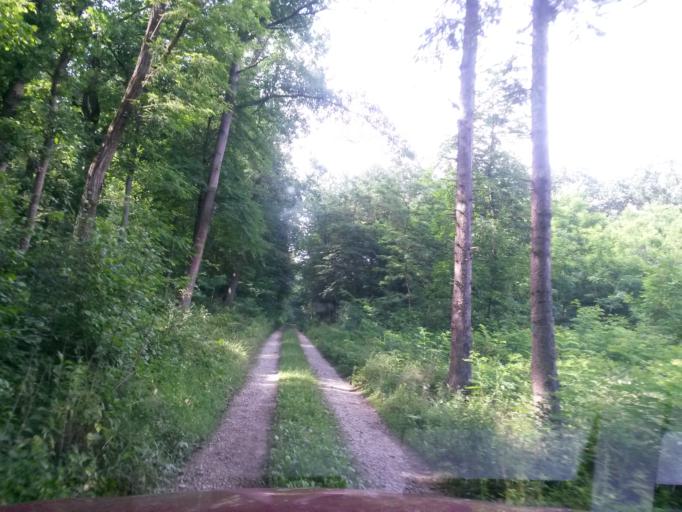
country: SK
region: Kosicky
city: Moldava nad Bodvou
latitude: 48.6124
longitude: 21.1128
